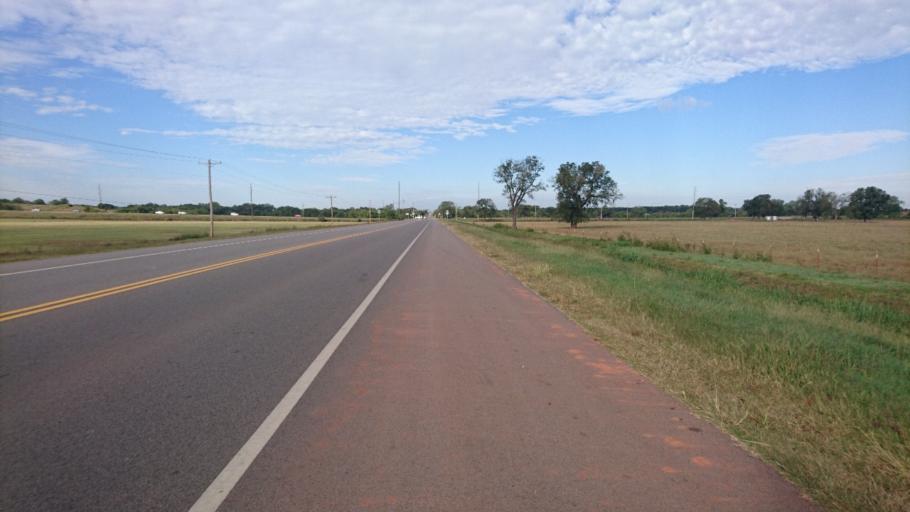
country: US
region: Oklahoma
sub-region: Lincoln County
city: Chandler
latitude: 35.6812
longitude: -97.0124
